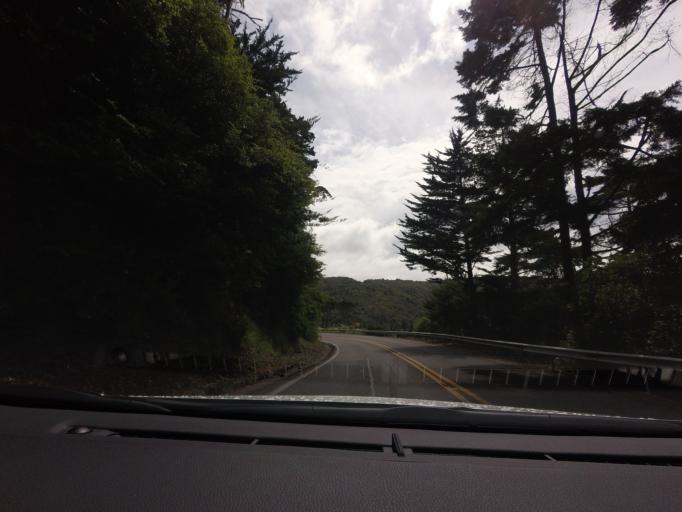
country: NZ
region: Auckland
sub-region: Auckland
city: Warkworth
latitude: -36.5450
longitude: 174.7044
